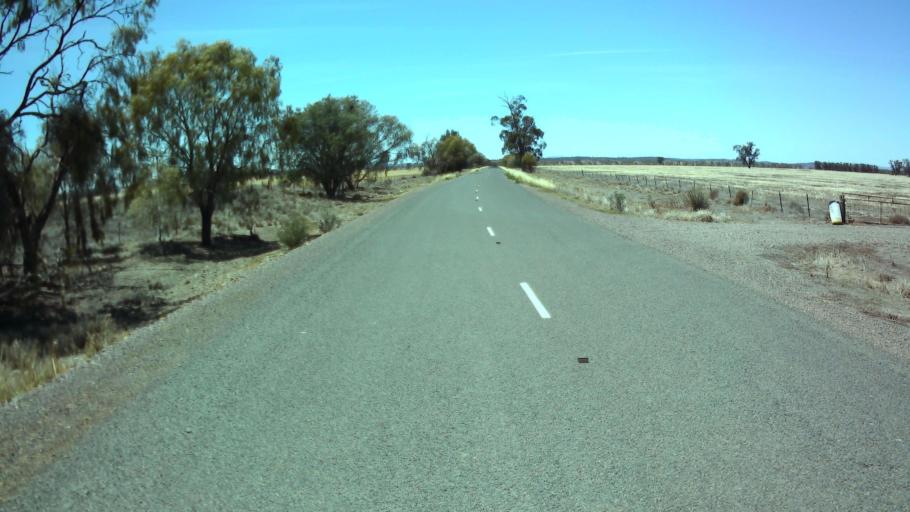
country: AU
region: New South Wales
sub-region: Bland
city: West Wyalong
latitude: -33.6606
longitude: 147.6047
